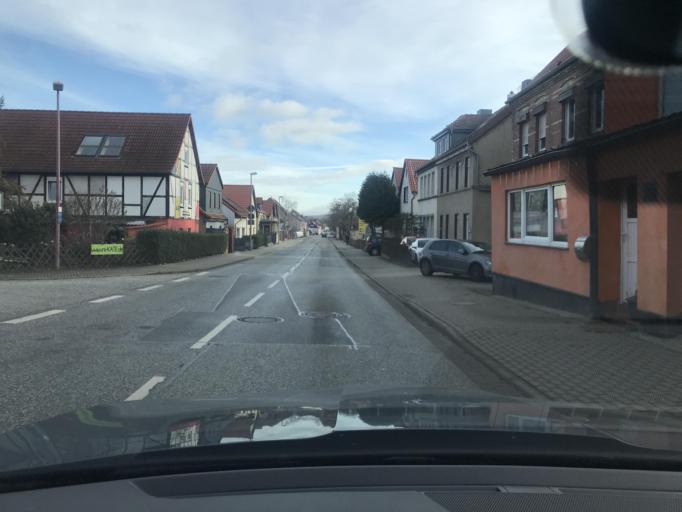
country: DE
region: Saxony-Anhalt
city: Thale
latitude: 51.7580
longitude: 11.0387
